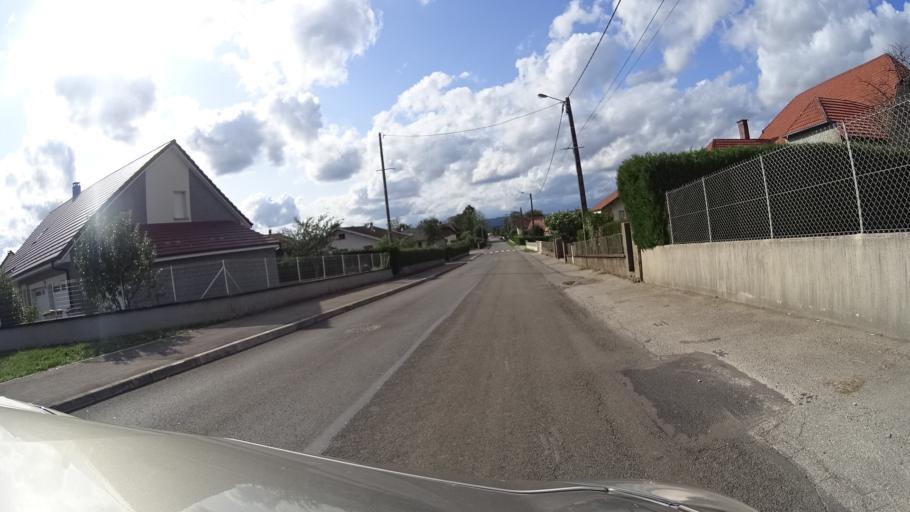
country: FR
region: Franche-Comte
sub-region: Departement du Doubs
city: Mamirolle
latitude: 47.2011
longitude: 6.1584
